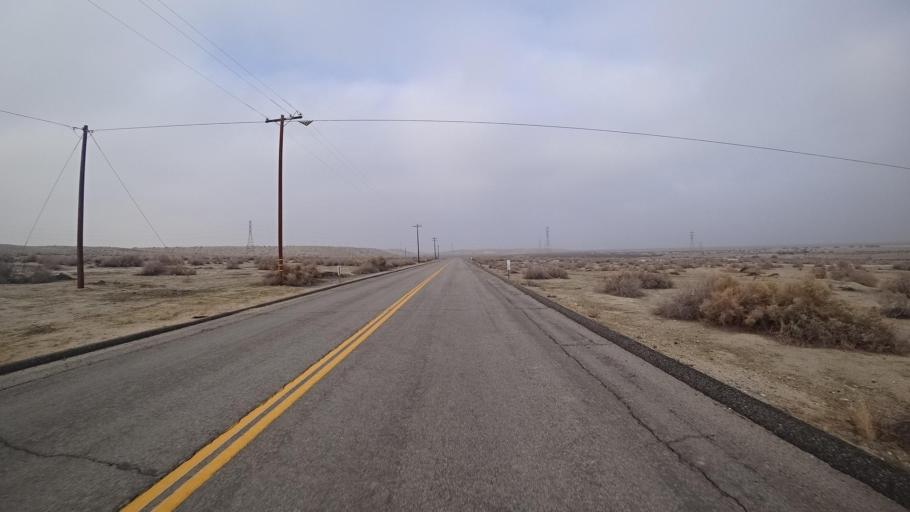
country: US
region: California
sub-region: Kern County
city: Maricopa
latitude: 35.1559
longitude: -119.3360
